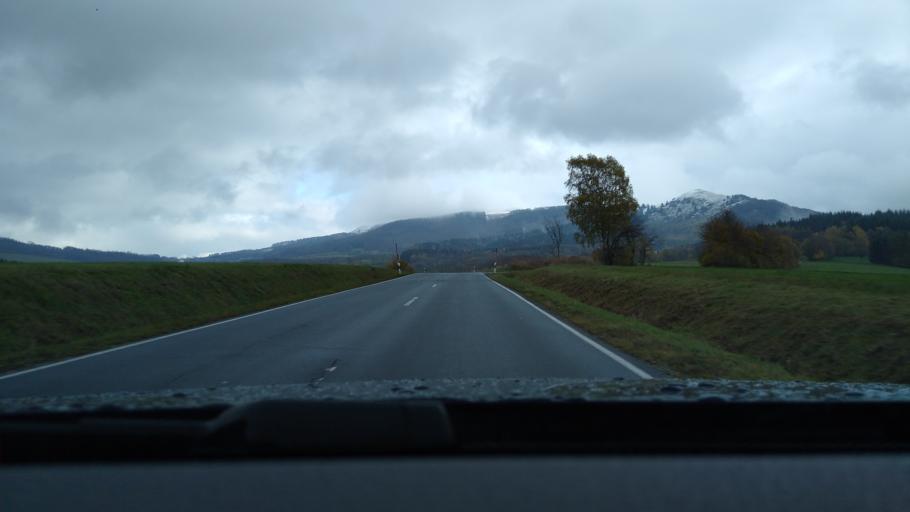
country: DE
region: Hesse
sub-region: Regierungsbezirk Kassel
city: Poppenhausen
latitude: 50.4961
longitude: 9.8853
